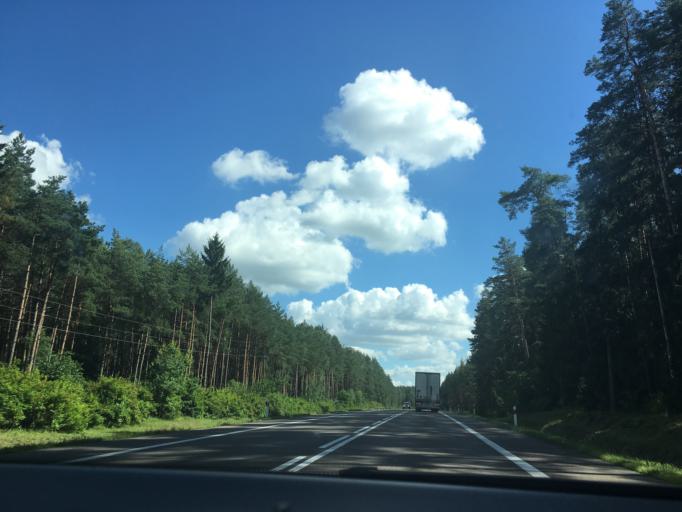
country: PL
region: Podlasie
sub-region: Powiat sokolski
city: Suchowola
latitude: 53.7316
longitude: 23.1032
